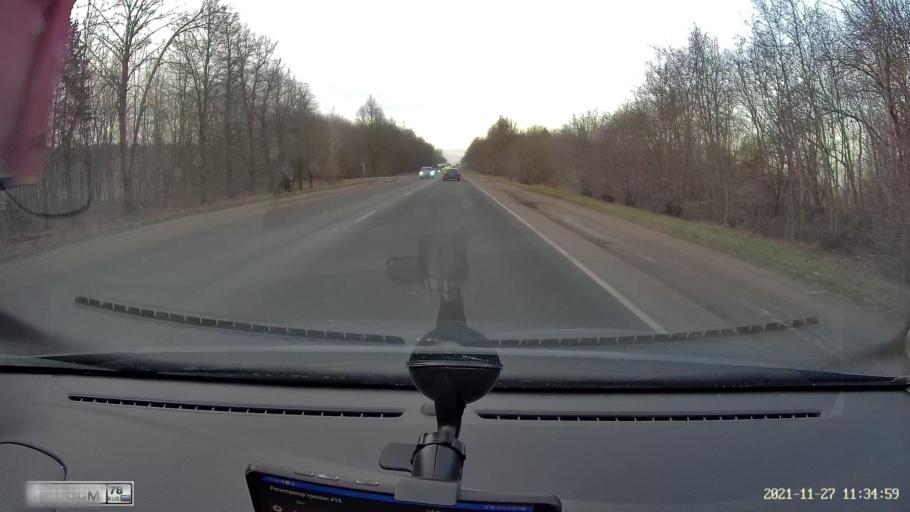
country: RU
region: Leningrad
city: Russko-Vysotskoye
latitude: 59.7042
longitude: 29.9898
